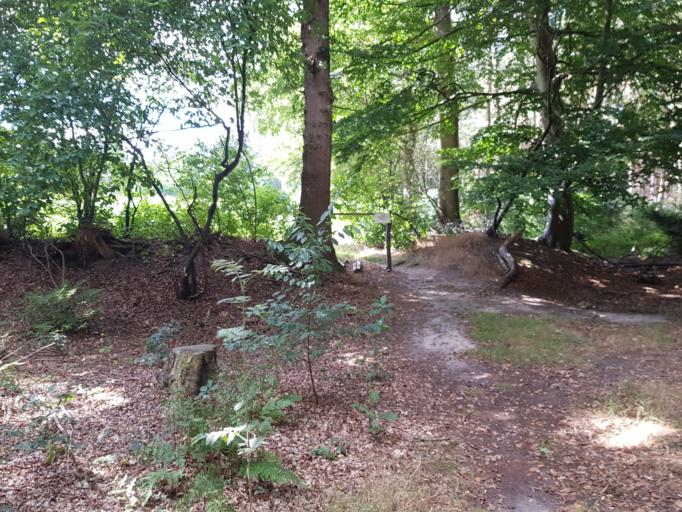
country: NL
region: Gelderland
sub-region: Gemeente Lochem
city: Lochem
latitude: 52.1187
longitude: 6.3578
